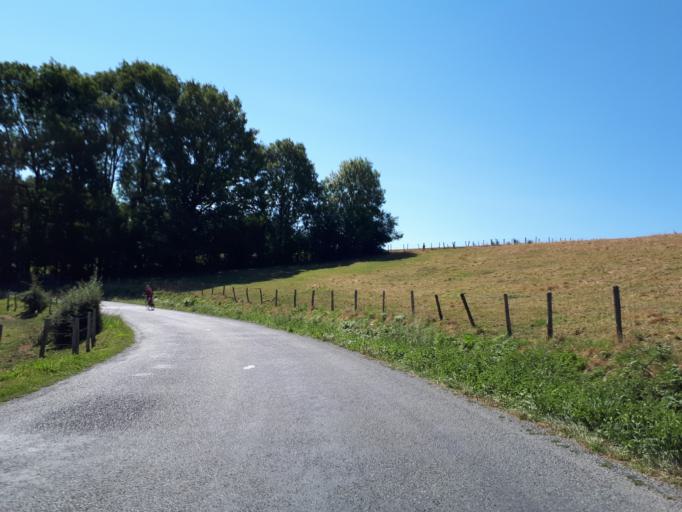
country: FR
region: Rhone-Alpes
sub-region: Departement de la Loire
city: Rozier-en-Donzy
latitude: 45.8178
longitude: 4.3074
